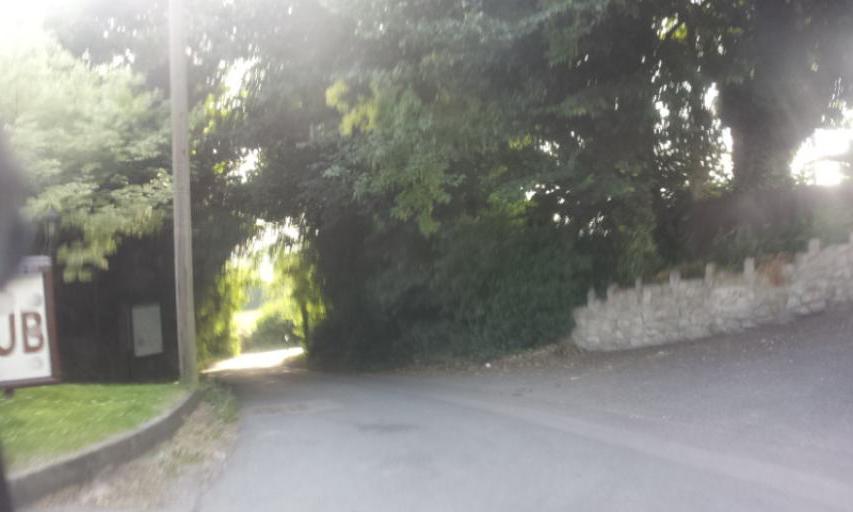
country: GB
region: England
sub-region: Kent
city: Boxley
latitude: 51.2914
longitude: 0.5893
